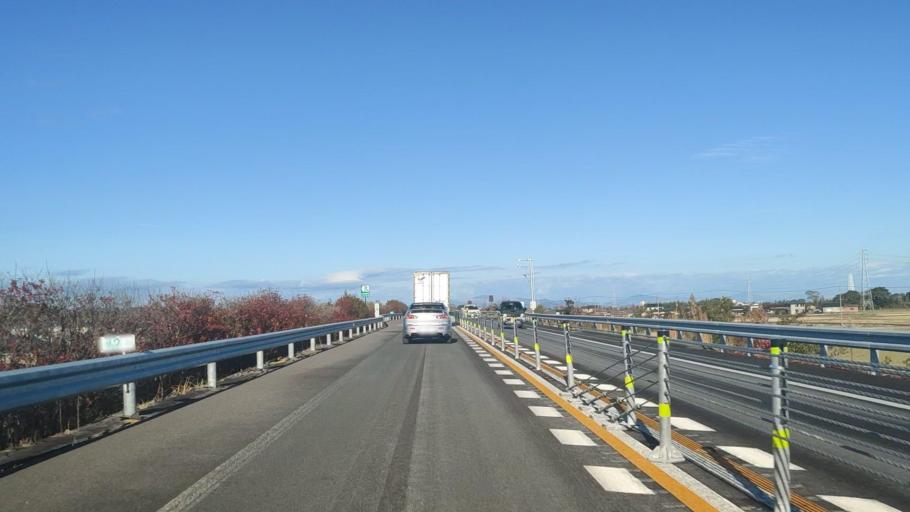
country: JP
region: Fukuoka
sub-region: Buzen-shi
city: Buzen
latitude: 33.5772
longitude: 131.1412
